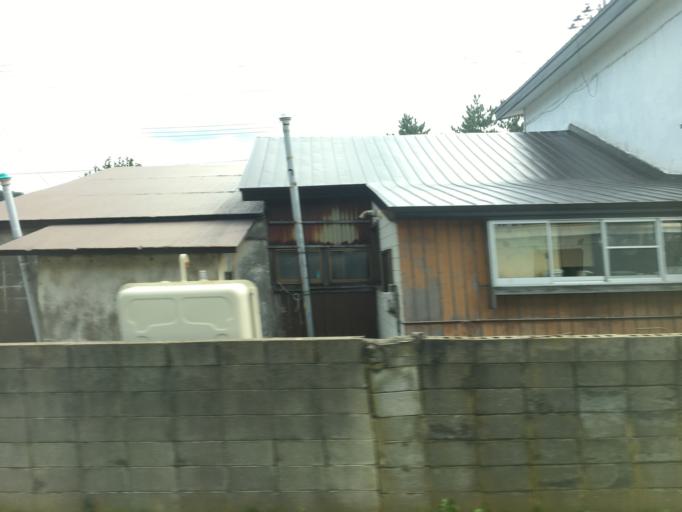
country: JP
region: Aomori
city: Shimokizukuri
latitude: 40.7633
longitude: 140.1640
